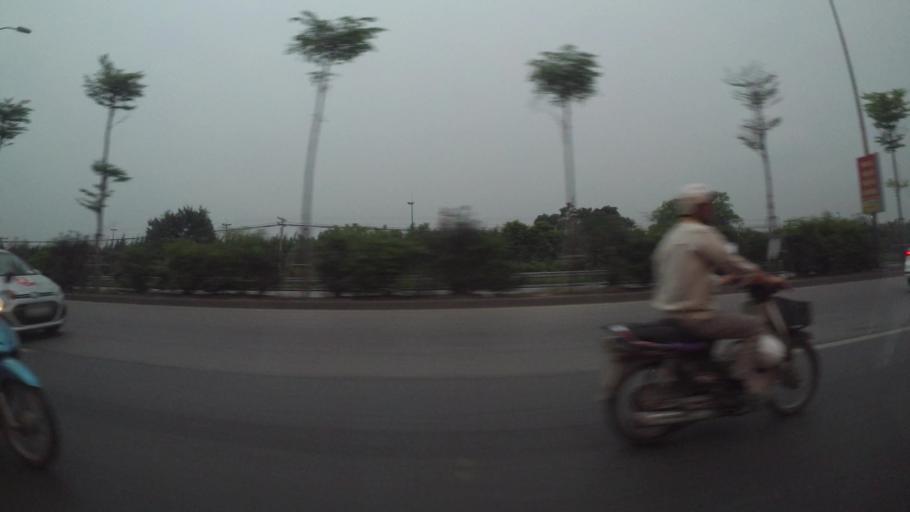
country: VN
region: Ha Noi
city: Trau Quy
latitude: 21.0438
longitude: 105.8961
